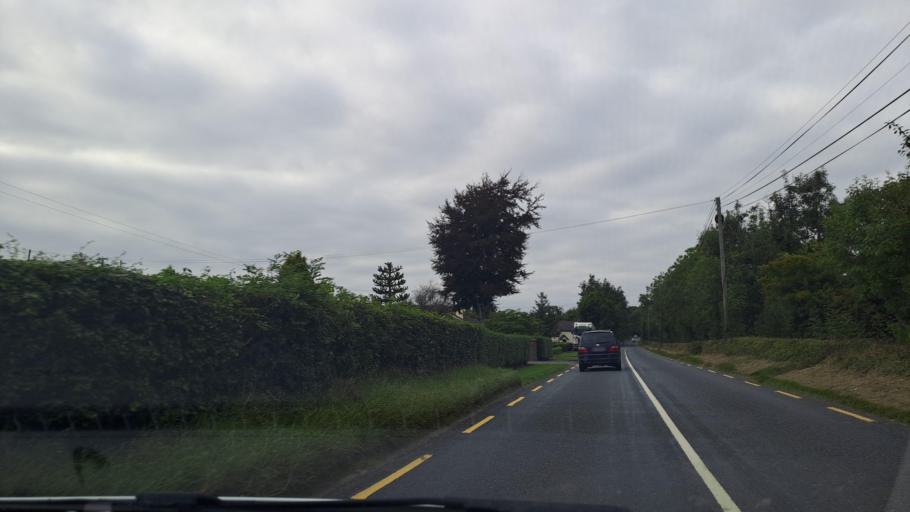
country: IE
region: Ulster
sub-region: County Monaghan
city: Carrickmacross
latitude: 54.0047
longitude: -6.7439
